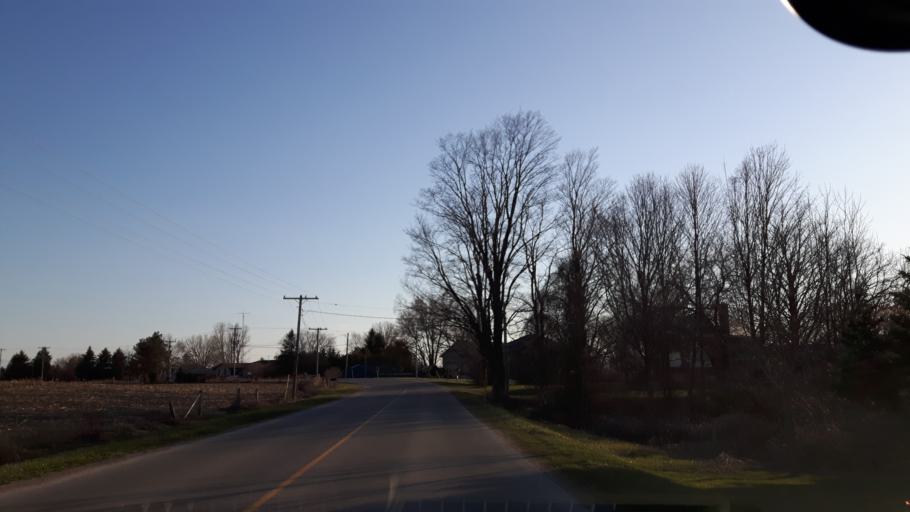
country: CA
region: Ontario
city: Goderich
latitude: 43.7210
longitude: -81.6844
